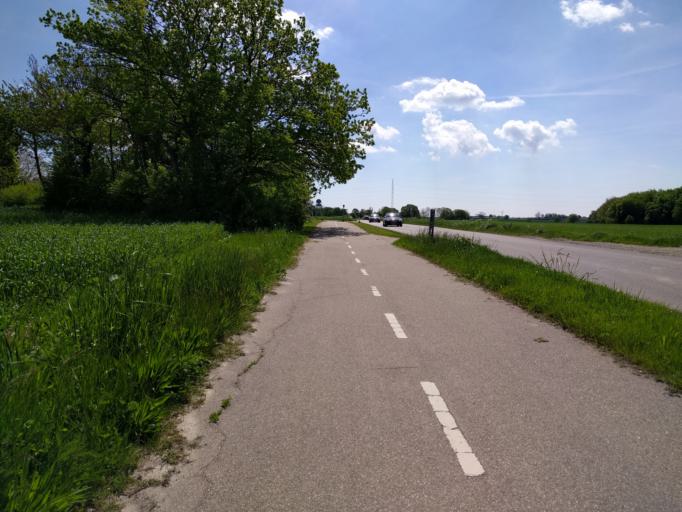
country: DK
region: Zealand
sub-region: Guldborgsund Kommune
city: Nykobing Falster
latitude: 54.7498
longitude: 11.9362
